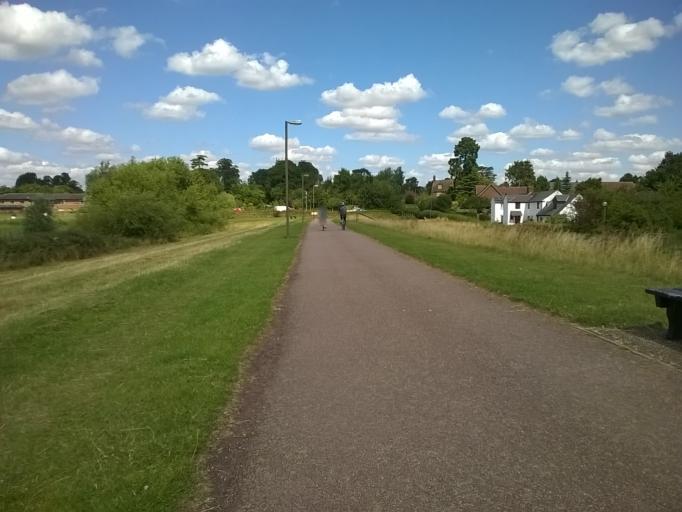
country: GB
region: England
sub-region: Milton Keynes
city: Broughton
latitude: 52.0604
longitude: -0.7182
